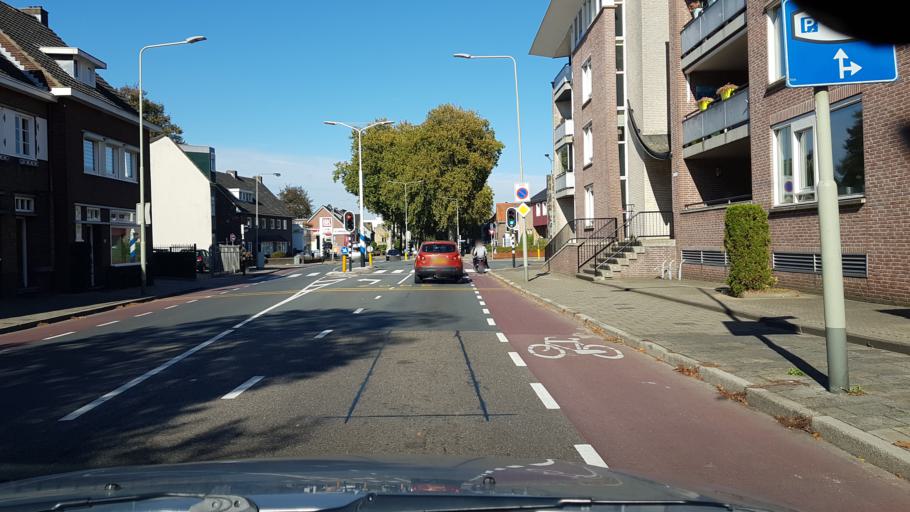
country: NL
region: Limburg
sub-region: Gemeente Beek
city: Beek
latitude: 50.9685
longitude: 5.8238
